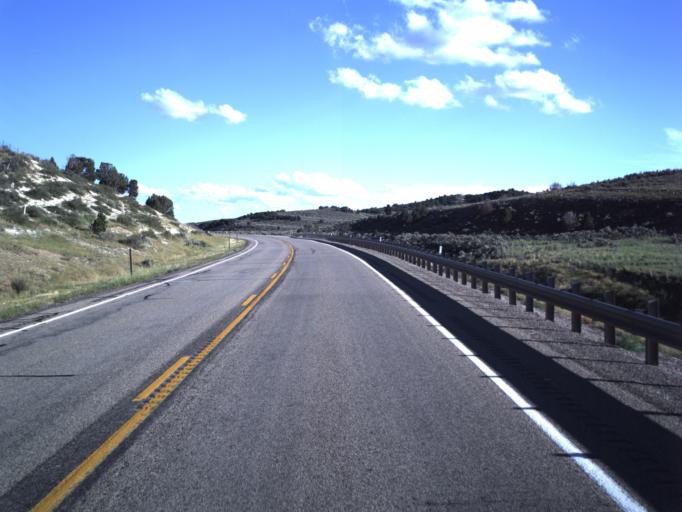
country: US
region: Utah
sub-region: Sanpete County
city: Fairview
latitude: 39.7357
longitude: -111.4771
